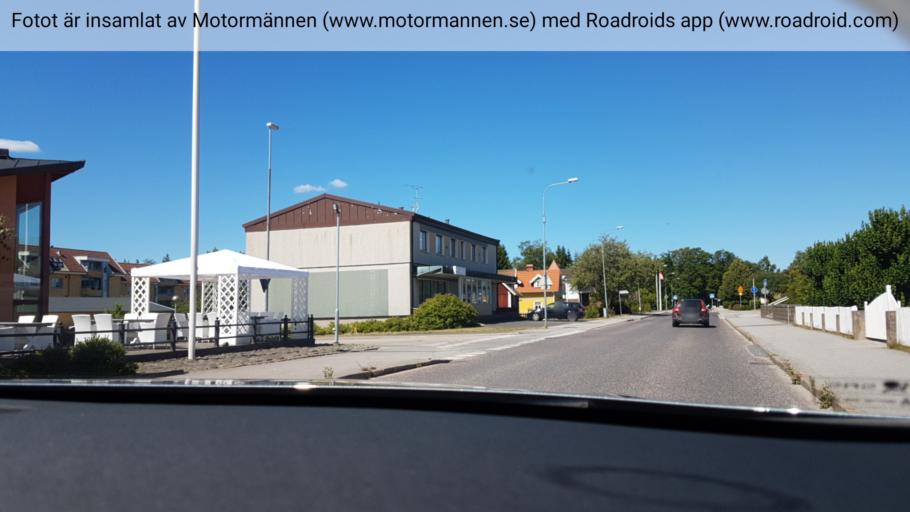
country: SE
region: Joenkoeping
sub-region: Gnosjo Kommun
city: Hillerstorp
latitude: 57.3151
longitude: 13.8806
